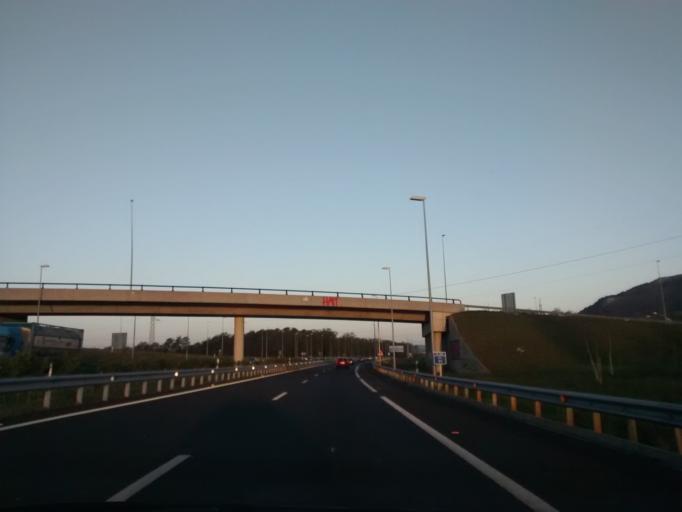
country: ES
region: Cantabria
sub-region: Provincia de Cantabria
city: El Astillero
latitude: 43.3907
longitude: -3.8323
